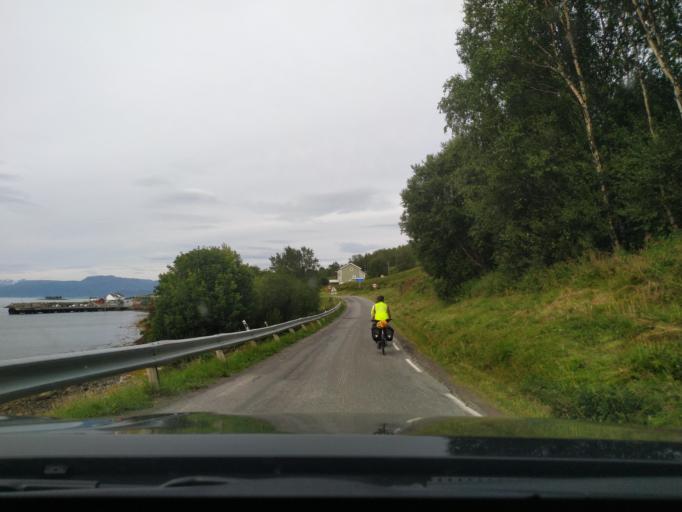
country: NO
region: Nordland
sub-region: Evenes
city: Randa
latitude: 68.7272
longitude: 16.8601
